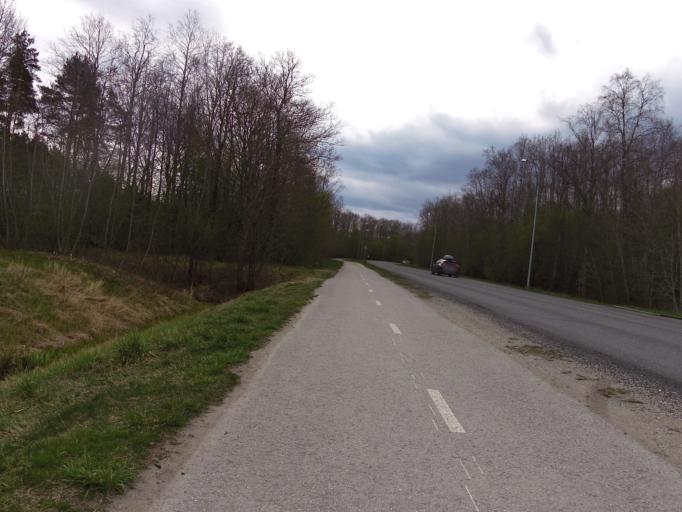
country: EE
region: Harju
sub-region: Kiili vald
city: Kiili
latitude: 59.3647
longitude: 24.8162
